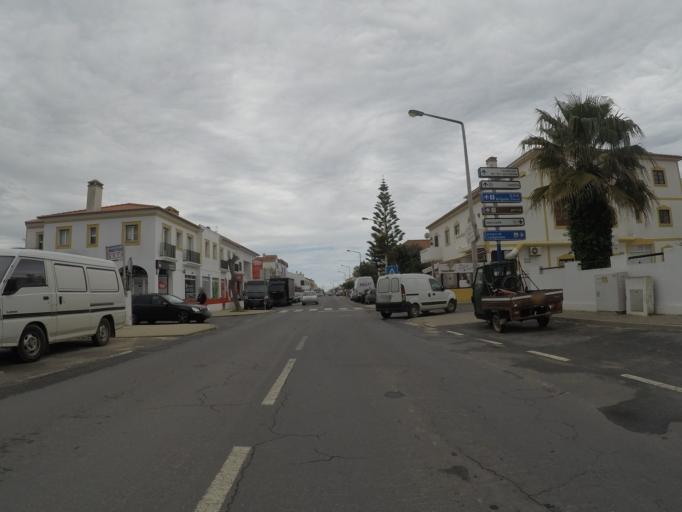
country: PT
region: Beja
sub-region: Odemira
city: Vila Nova de Milfontes
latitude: 37.7289
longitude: -8.7770
